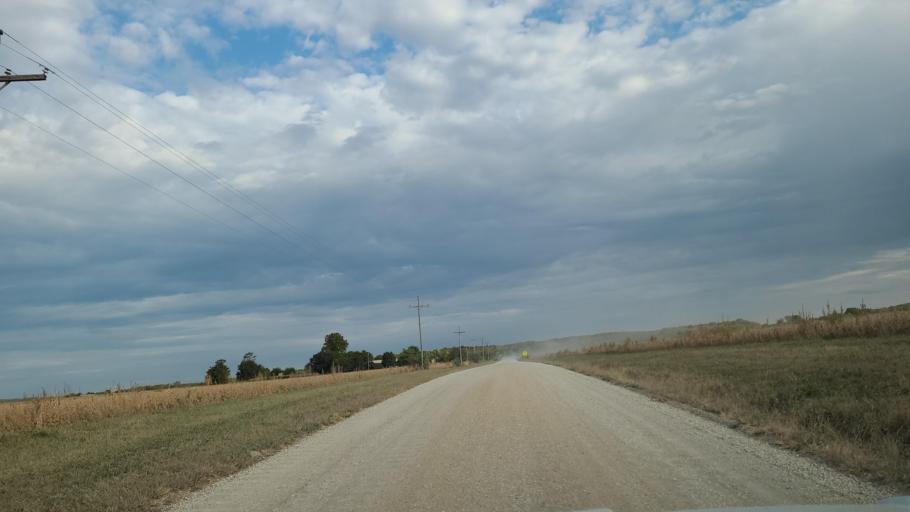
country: US
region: Kansas
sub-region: Douglas County
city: Lawrence
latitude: 39.0051
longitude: -95.2055
